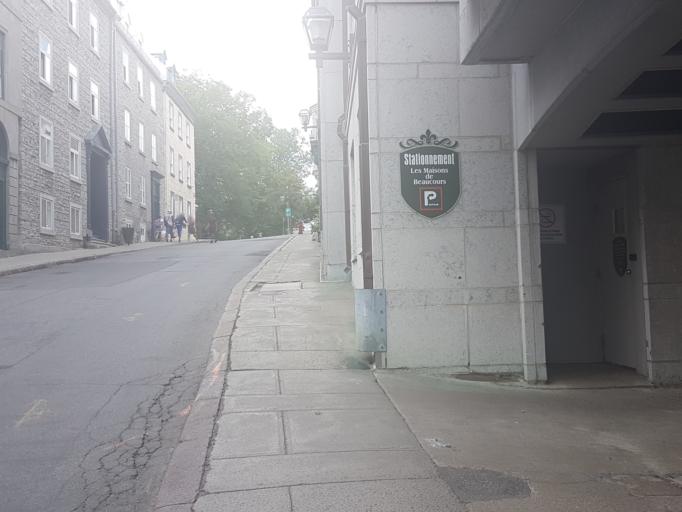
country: CA
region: Quebec
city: Quebec
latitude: 46.8115
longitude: -71.2069
